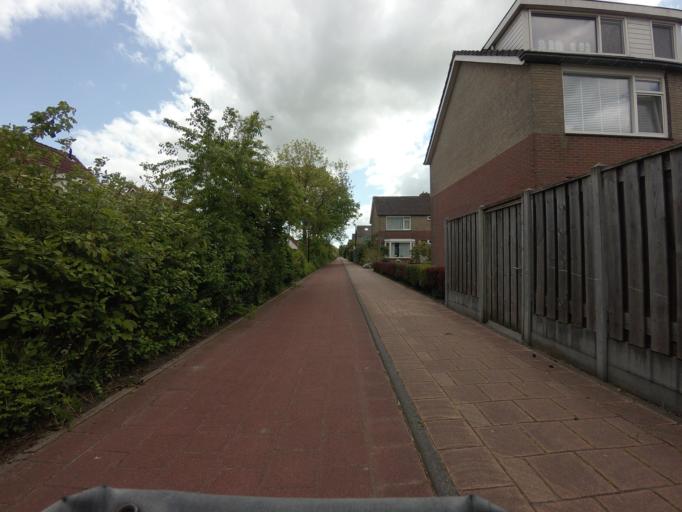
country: NL
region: Friesland
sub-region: Sudwest Fryslan
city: Bolsward
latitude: 53.0706
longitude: 5.5323
